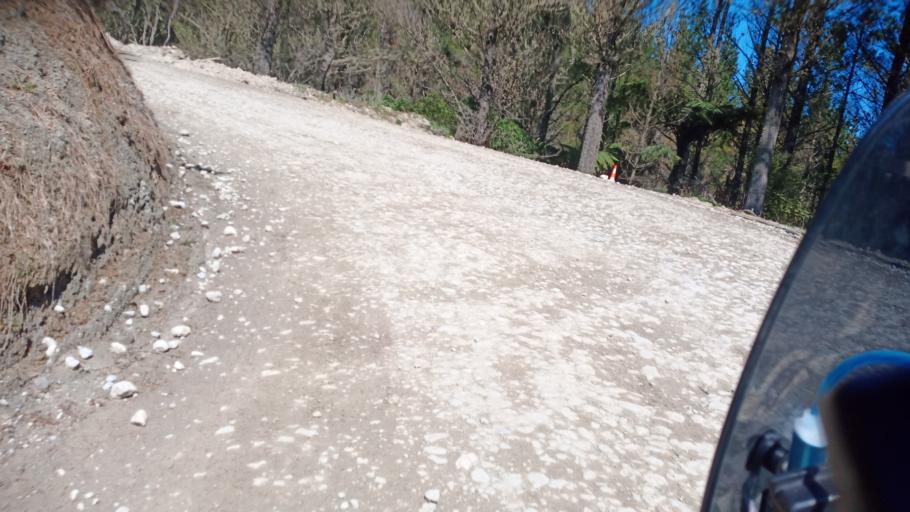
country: NZ
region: Gisborne
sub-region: Gisborne District
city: Gisborne
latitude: -38.8986
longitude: 177.8010
